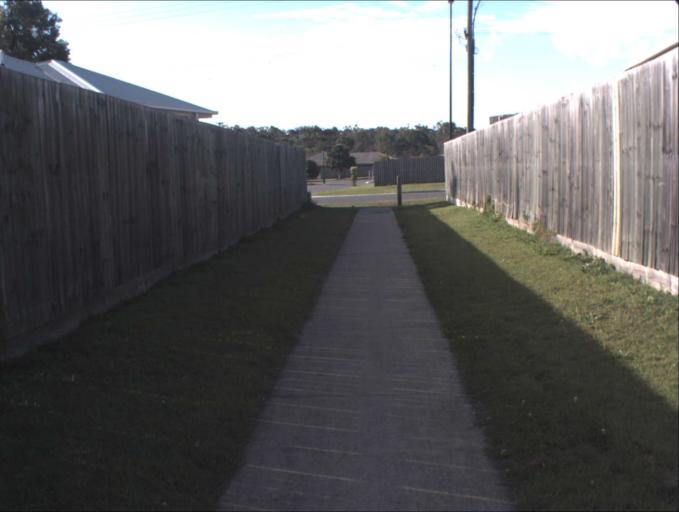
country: AU
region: Queensland
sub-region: Logan
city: Logan Reserve
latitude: -27.6948
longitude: 153.0925
